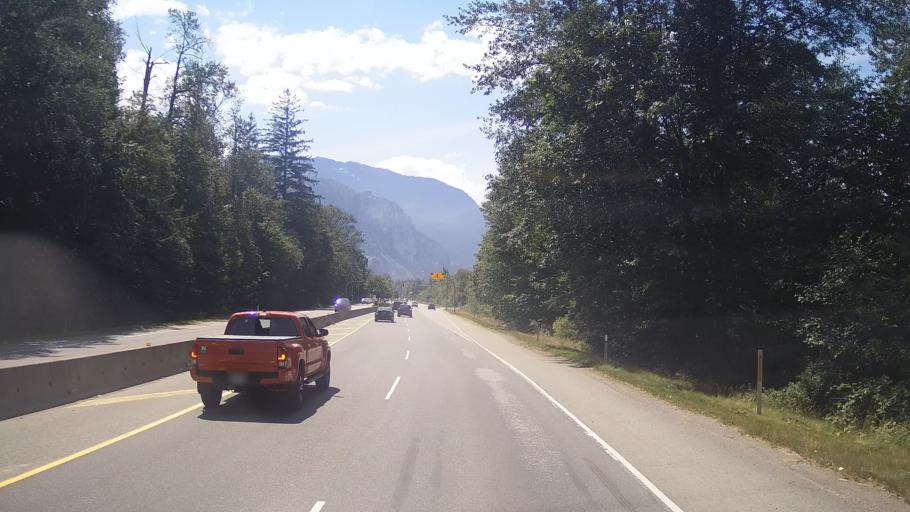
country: CA
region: British Columbia
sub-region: Greater Vancouver Regional District
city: Lions Bay
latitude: 49.7250
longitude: -123.1481
